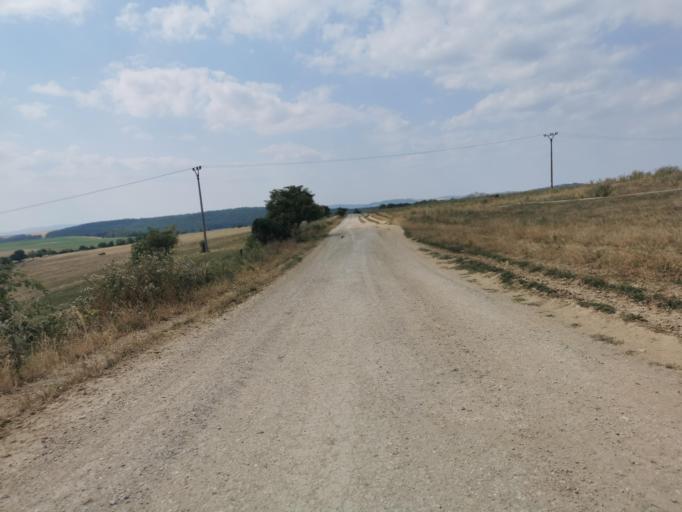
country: SK
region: Nitriansky
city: Brezova pod Bradlom
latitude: 48.7042
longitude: 17.5022
